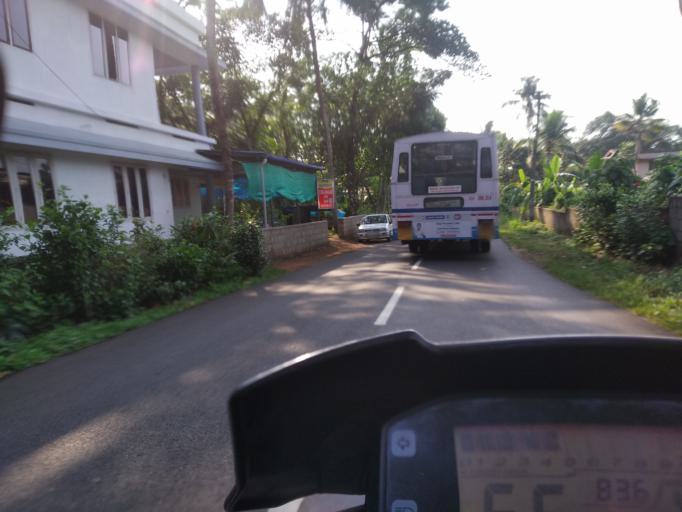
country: IN
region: Kerala
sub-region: Ernakulam
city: Ramamangalam
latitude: 9.9145
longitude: 76.4301
